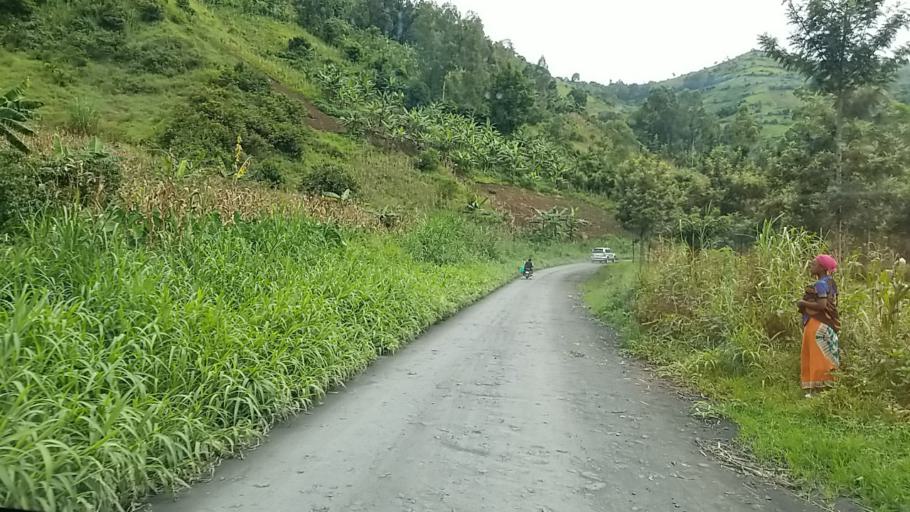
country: CD
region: Nord Kivu
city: Sake
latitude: -1.7356
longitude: 29.0072
